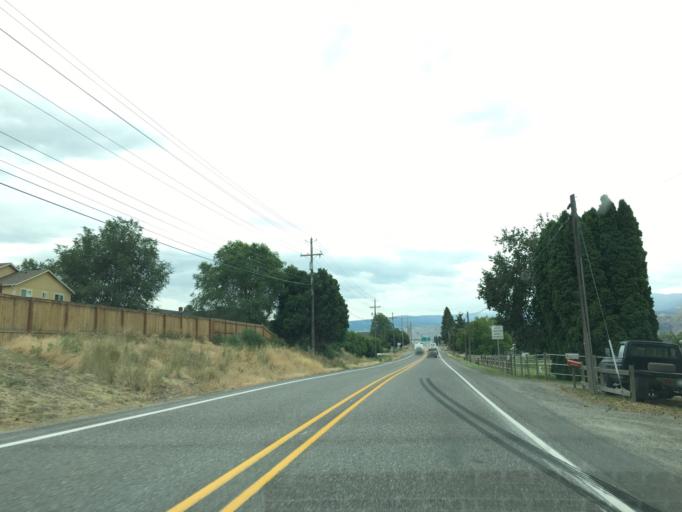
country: US
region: Washington
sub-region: Chelan County
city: Sunnyslope
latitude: 47.4754
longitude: -120.3004
